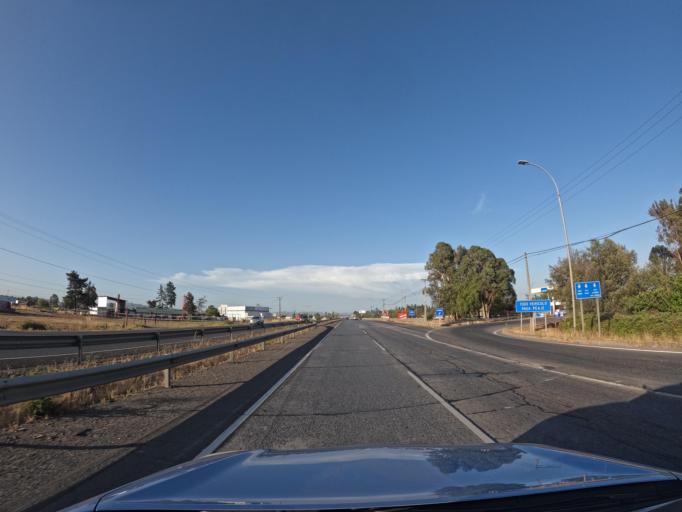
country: CL
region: Maule
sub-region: Provincia de Talca
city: Talca
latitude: -35.4897
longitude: -71.6600
